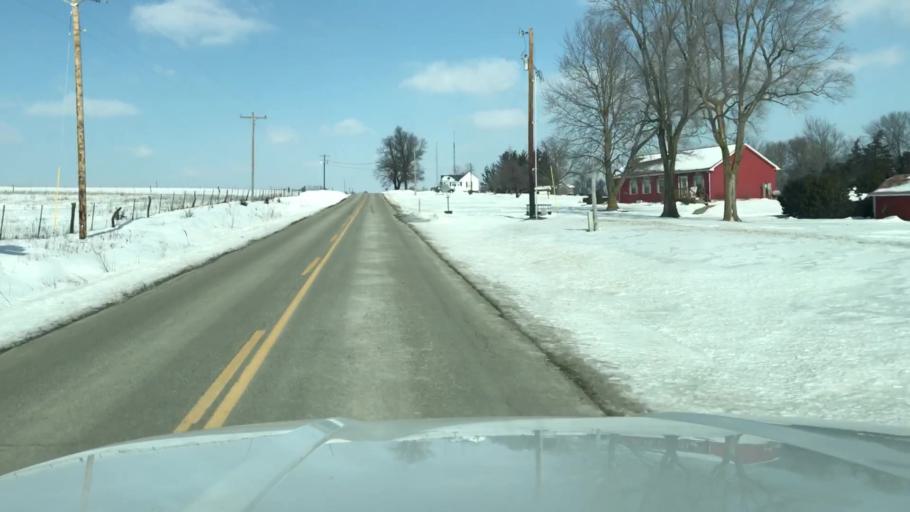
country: US
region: Missouri
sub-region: Nodaway County
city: Maryville
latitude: 40.3461
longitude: -94.7223
